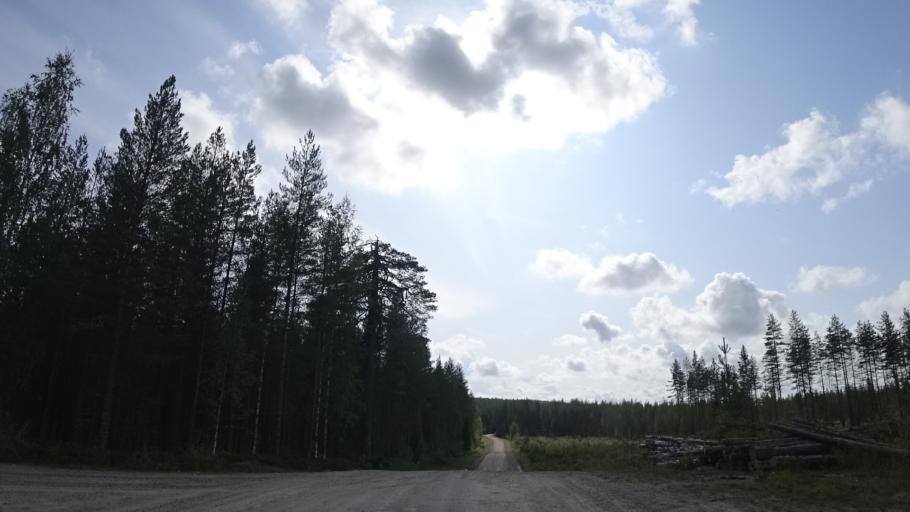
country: FI
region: North Karelia
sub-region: Pielisen Karjala
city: Lieksa
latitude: 63.5740
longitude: 30.1180
